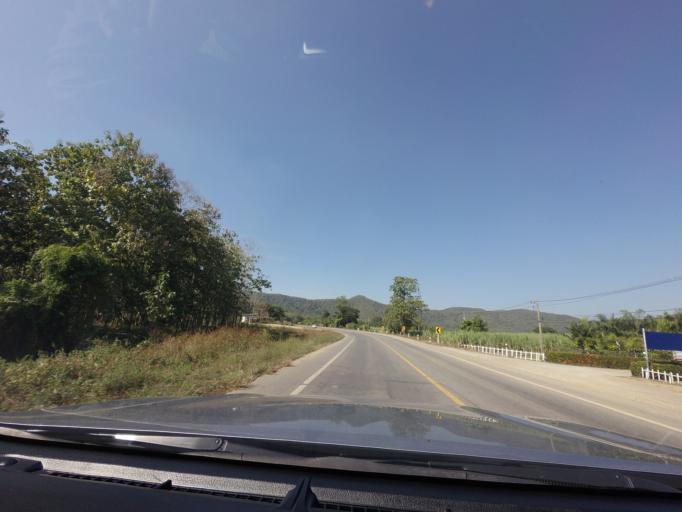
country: TH
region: Sukhothai
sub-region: Amphoe Si Satchanalai
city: Si Satchanalai
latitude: 17.5570
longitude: 99.7699
